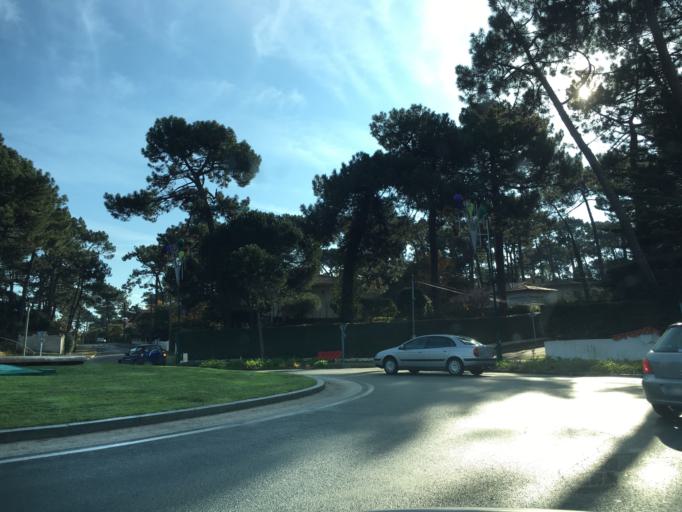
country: FR
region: Aquitaine
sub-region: Departement de la Gironde
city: Arcachon
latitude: 44.6477
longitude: -1.1842
